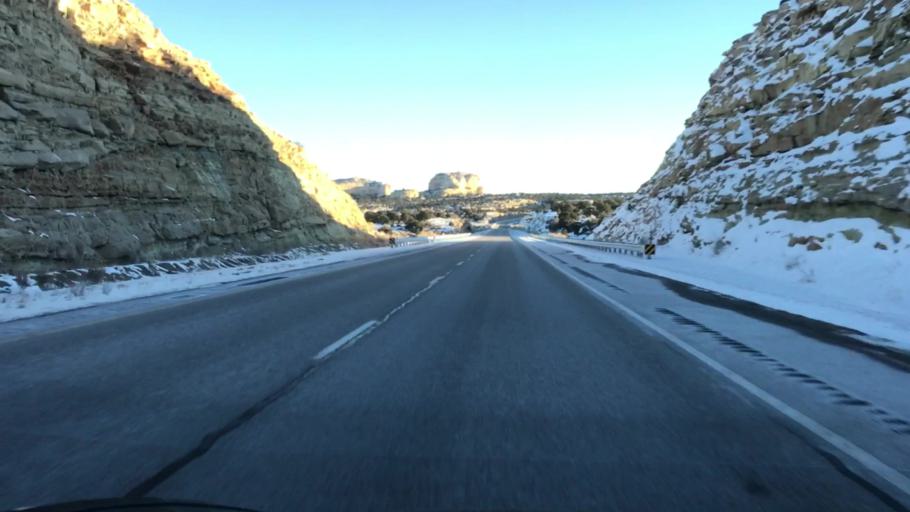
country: US
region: Utah
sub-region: Emery County
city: Ferron
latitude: 38.8566
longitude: -110.8692
